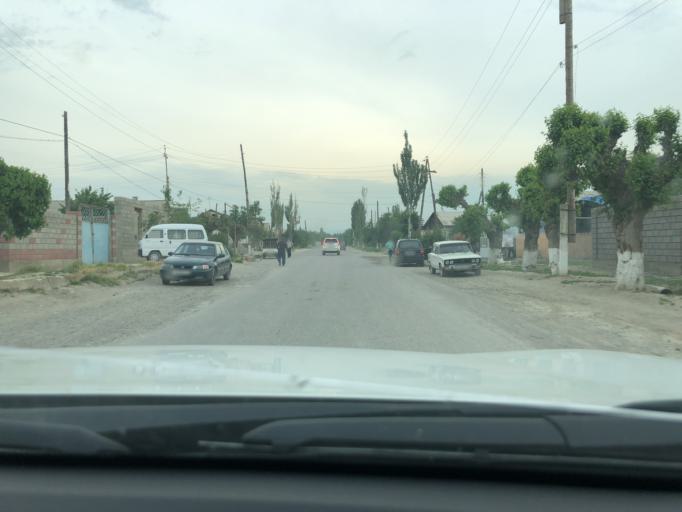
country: UZ
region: Toshkent
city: Bekobod
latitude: 40.1441
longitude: 69.2540
